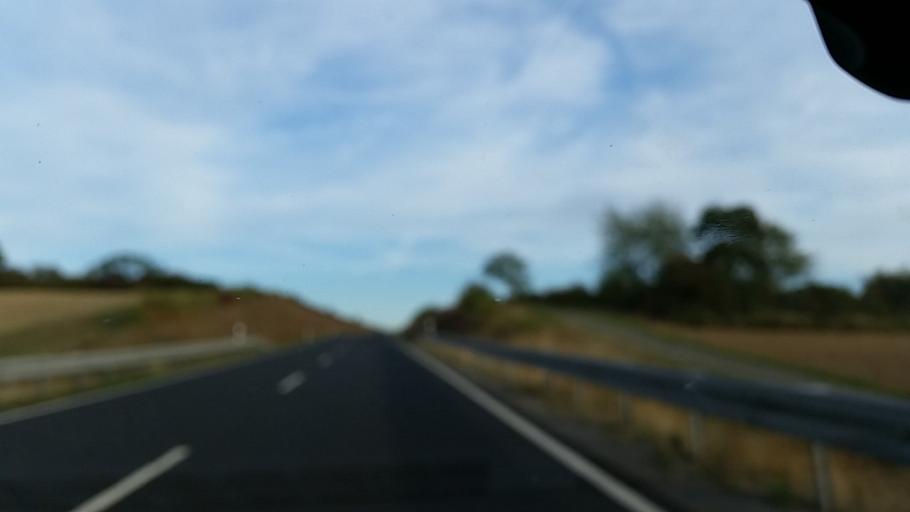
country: DE
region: Bavaria
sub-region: Regierungsbezirk Unterfranken
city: Mellrichstadt
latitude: 50.4407
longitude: 10.3171
